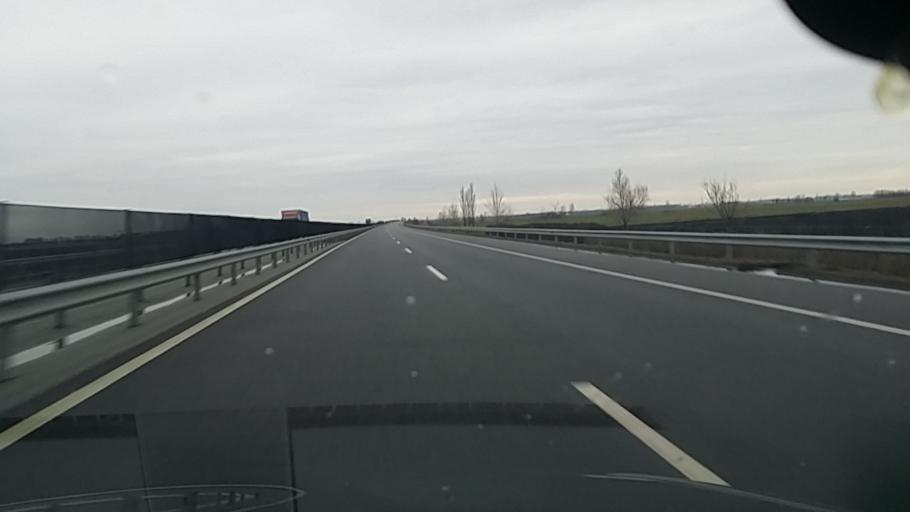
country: HU
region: Hajdu-Bihar
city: Hajdunanas
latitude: 47.8380
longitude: 21.3369
